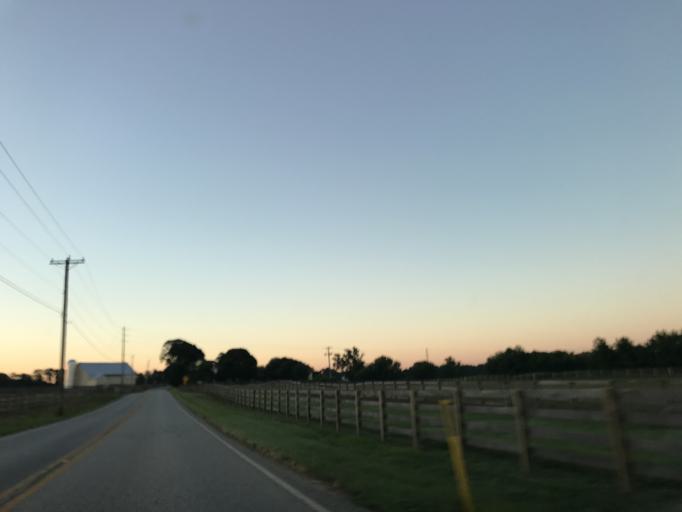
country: US
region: Pennsylvania
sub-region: Adams County
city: McSherrystown
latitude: 39.7844
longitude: -77.0324
